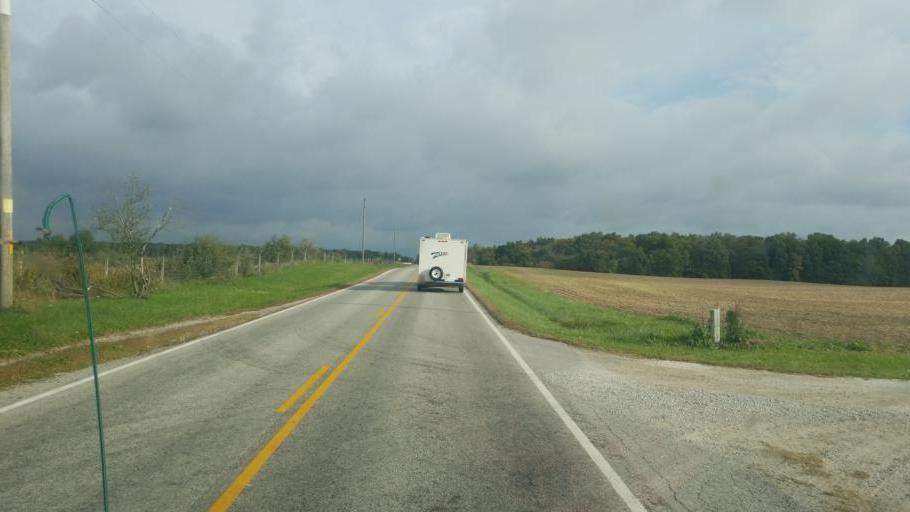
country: US
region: Ohio
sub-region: Seneca County
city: Fostoria
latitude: 41.0454
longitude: -83.4774
